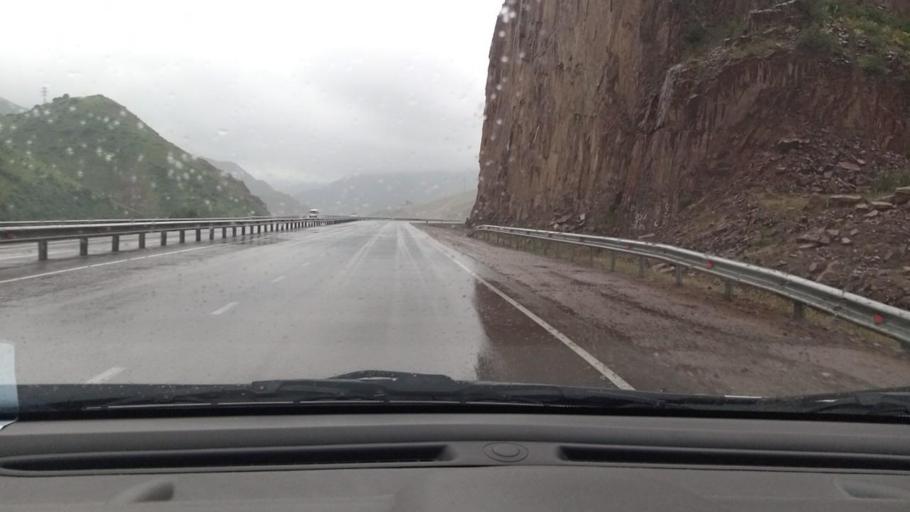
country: UZ
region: Toshkent
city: Angren
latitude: 41.1198
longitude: 70.3482
